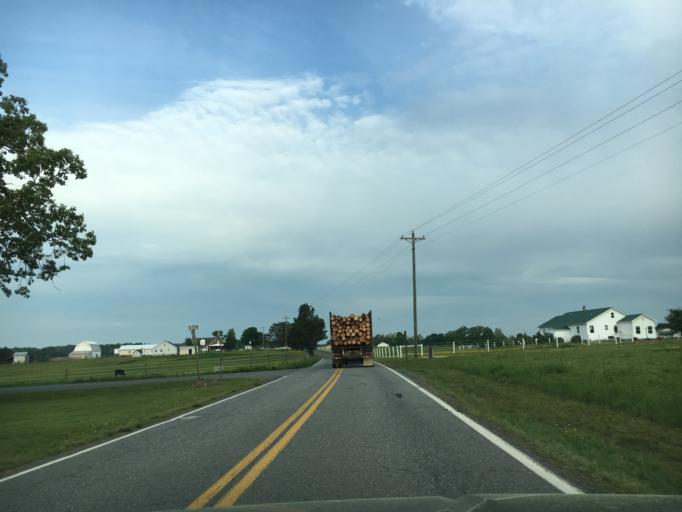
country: US
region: Virginia
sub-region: Halifax County
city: Halifax
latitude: 36.8990
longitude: -78.8632
